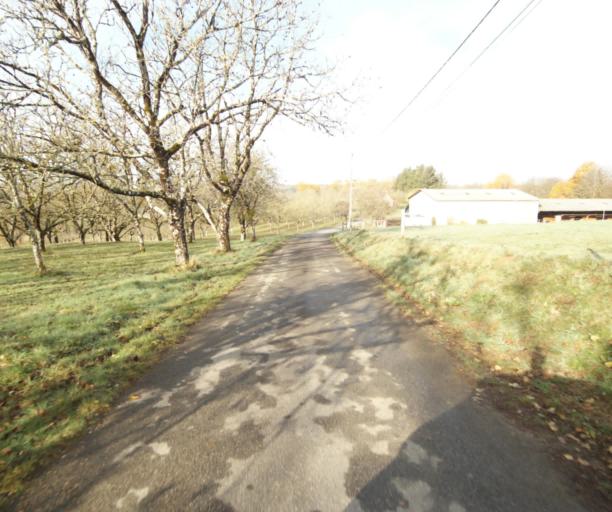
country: FR
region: Limousin
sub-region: Departement de la Correze
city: Sainte-Fortunade
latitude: 45.2245
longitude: 1.7391
